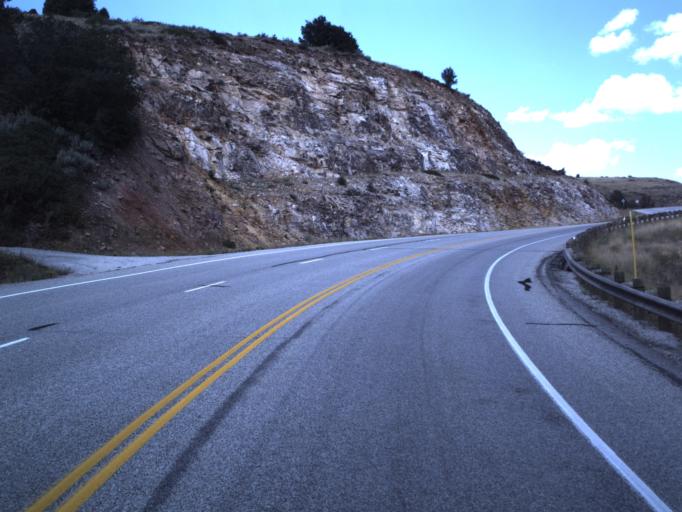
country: US
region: Idaho
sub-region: Bear Lake County
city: Paris
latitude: 41.9267
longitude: -111.4326
